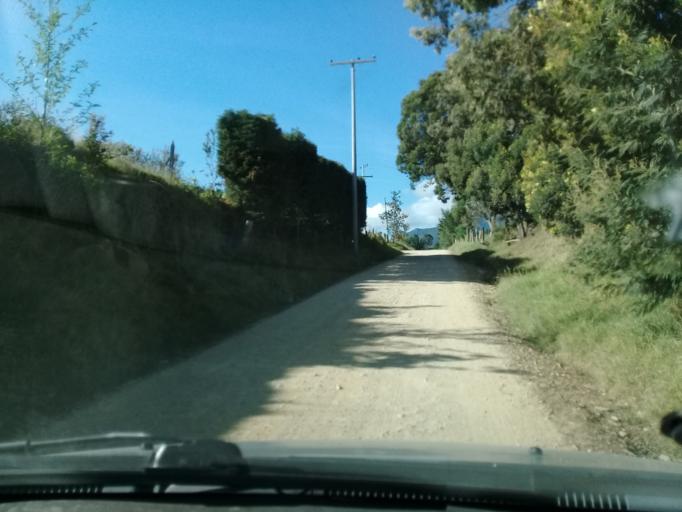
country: CO
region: Cundinamarca
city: Guatavita
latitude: 4.9366
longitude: -73.8777
